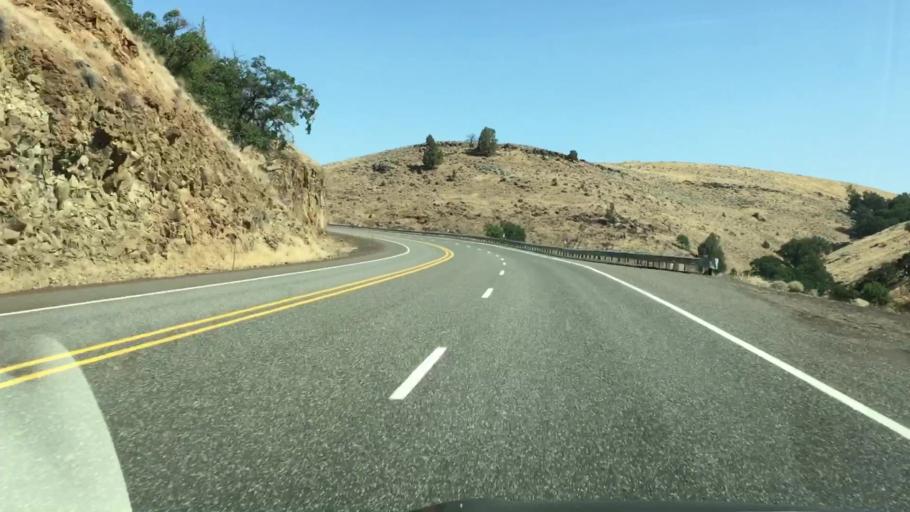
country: US
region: Oregon
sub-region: Wasco County
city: The Dalles
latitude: 45.3055
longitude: -121.1481
